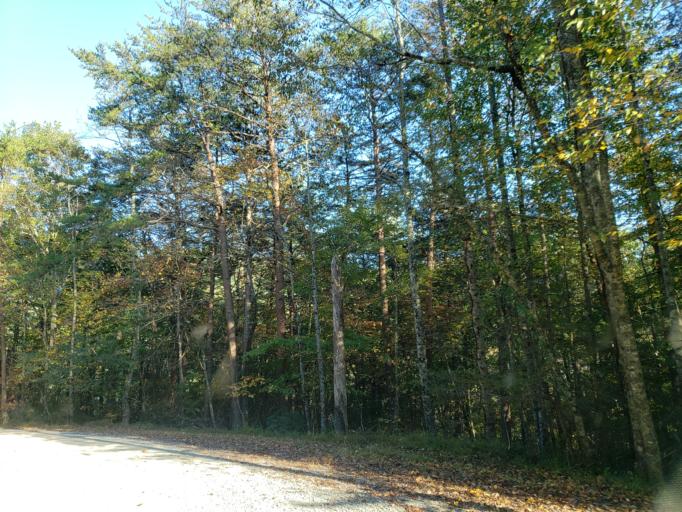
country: US
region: Georgia
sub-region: Fannin County
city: Blue Ridge
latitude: 34.6513
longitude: -84.2610
